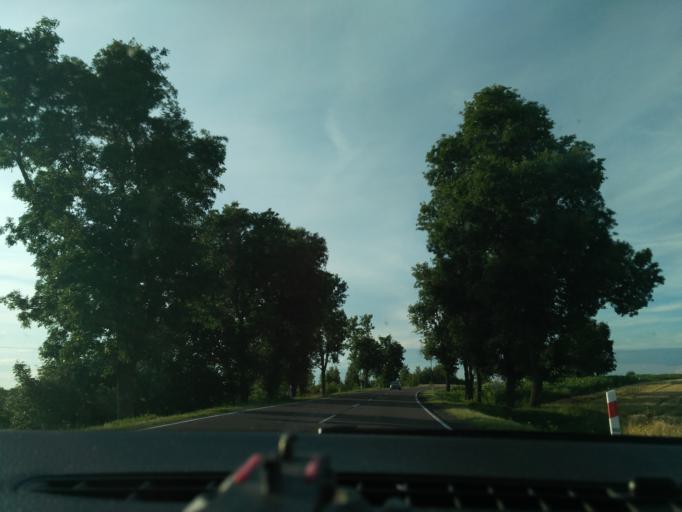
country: PL
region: Lublin Voivodeship
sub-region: Powiat krasnicki
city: Krasnik
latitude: 50.8833
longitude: 22.2608
